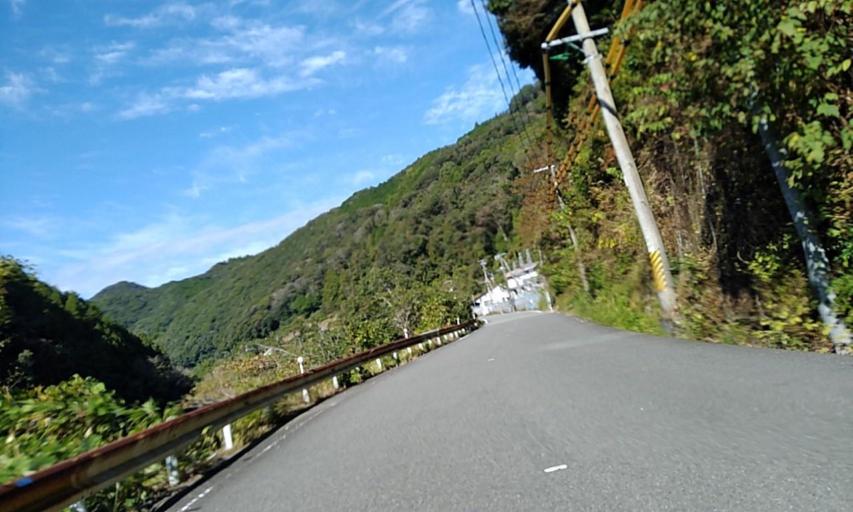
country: JP
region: Wakayama
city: Kainan
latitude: 34.0550
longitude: 135.3405
